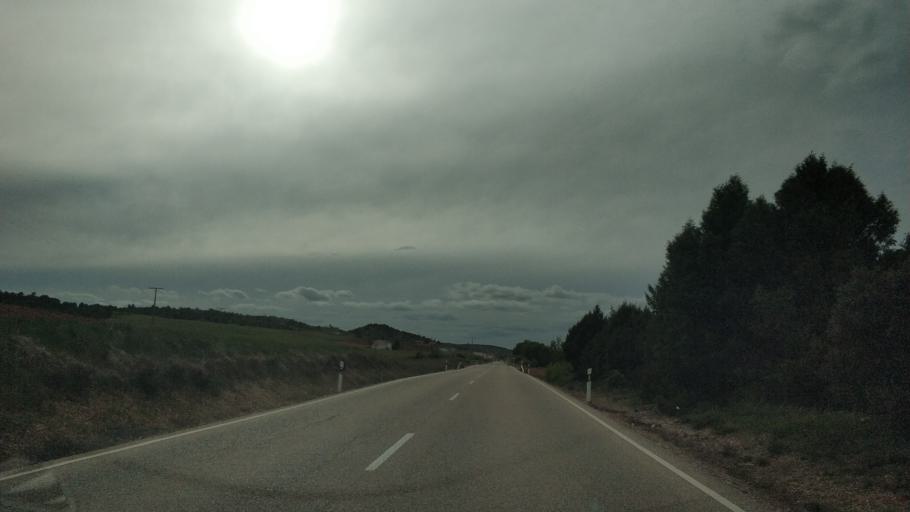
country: ES
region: Castille and Leon
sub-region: Provincia de Soria
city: Valdenebro
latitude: 41.5672
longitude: -3.0017
